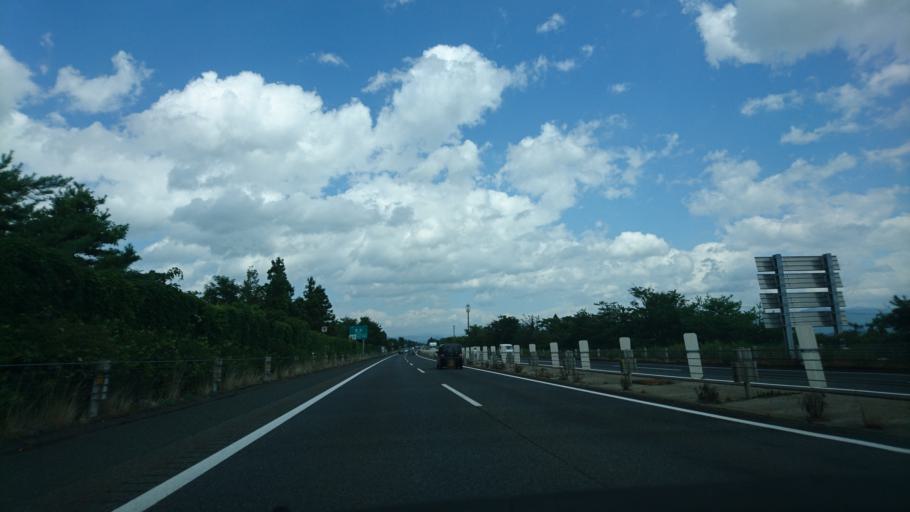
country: JP
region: Iwate
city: Hanamaki
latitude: 39.5457
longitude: 141.1076
